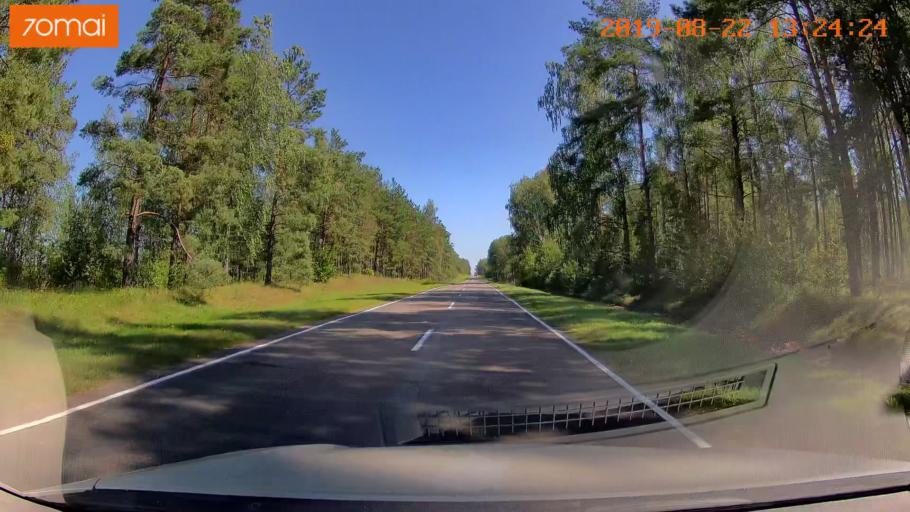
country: BY
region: Minsk
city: Urechcha
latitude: 53.2110
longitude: 28.0203
